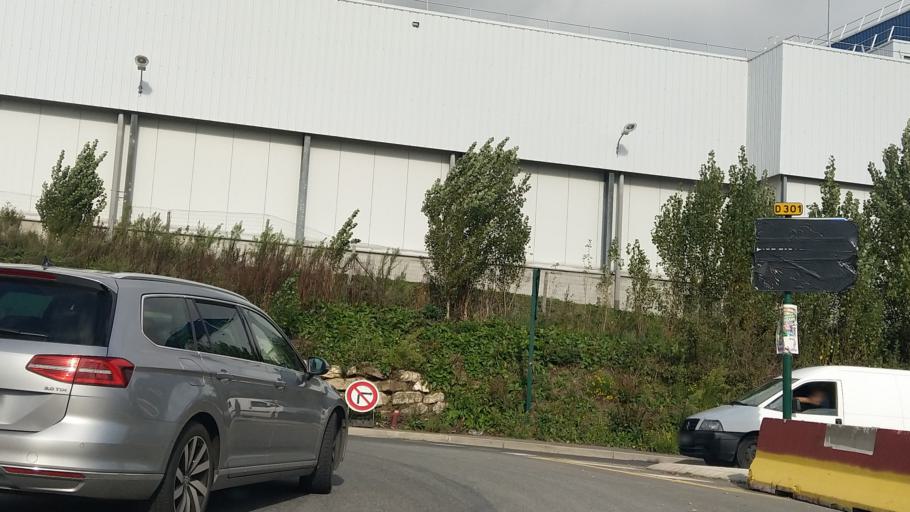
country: FR
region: Ile-de-France
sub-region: Departement du Val-d'Oise
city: Montsoult
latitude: 49.0636
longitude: 2.3273
